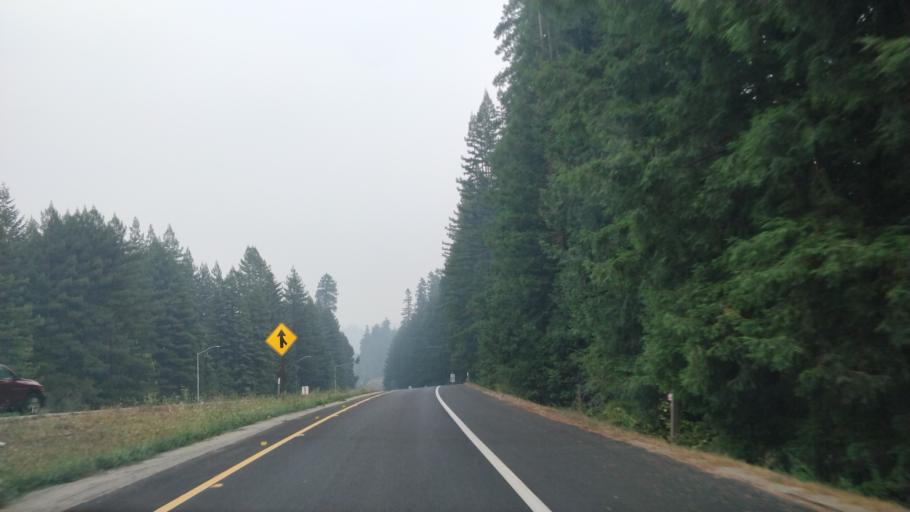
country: US
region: California
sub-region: Humboldt County
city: Rio Dell
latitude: 40.3970
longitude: -123.9473
